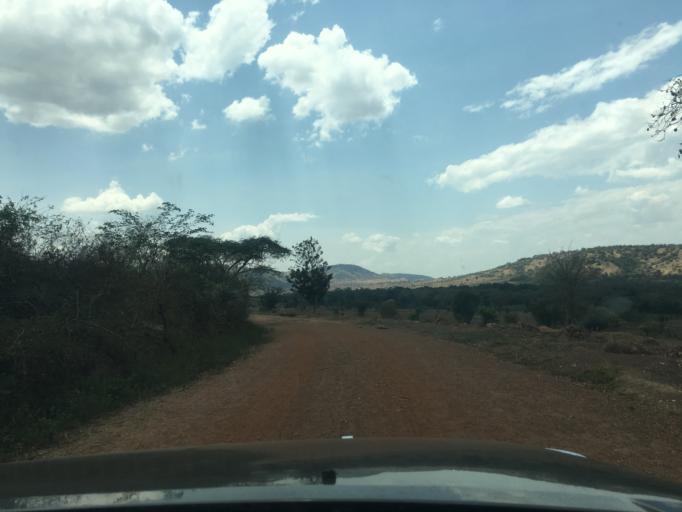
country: RW
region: Eastern Province
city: Kibungo
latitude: -2.1195
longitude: 30.8524
